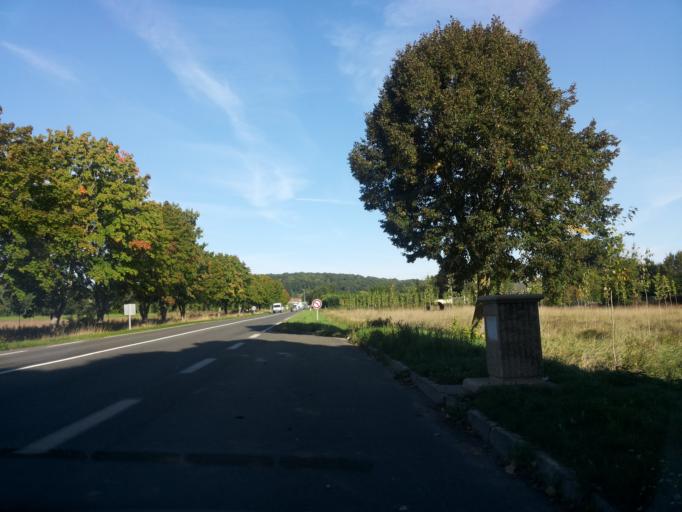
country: FR
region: Picardie
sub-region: Departement de l'Aisne
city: Crepy
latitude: 49.6034
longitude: 3.5097
